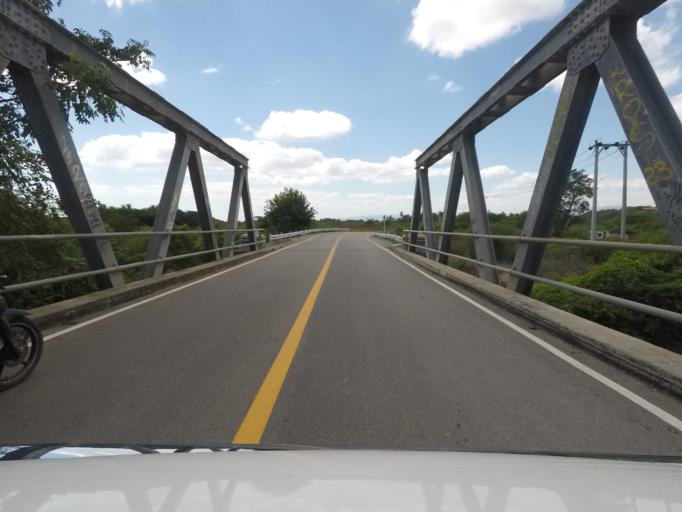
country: TL
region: Baucau
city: Baucau
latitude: -8.4086
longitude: 126.7307
